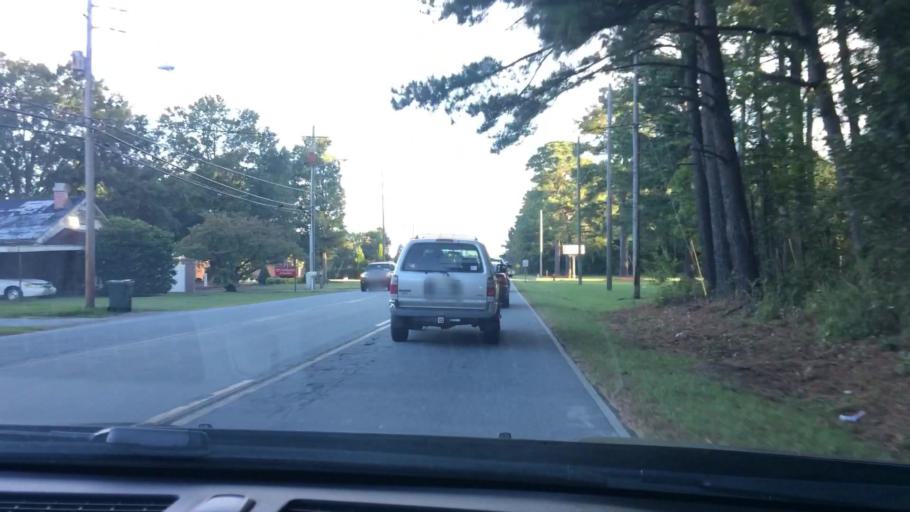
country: US
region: North Carolina
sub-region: Pitt County
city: Summerfield
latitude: 35.5707
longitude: -77.3827
